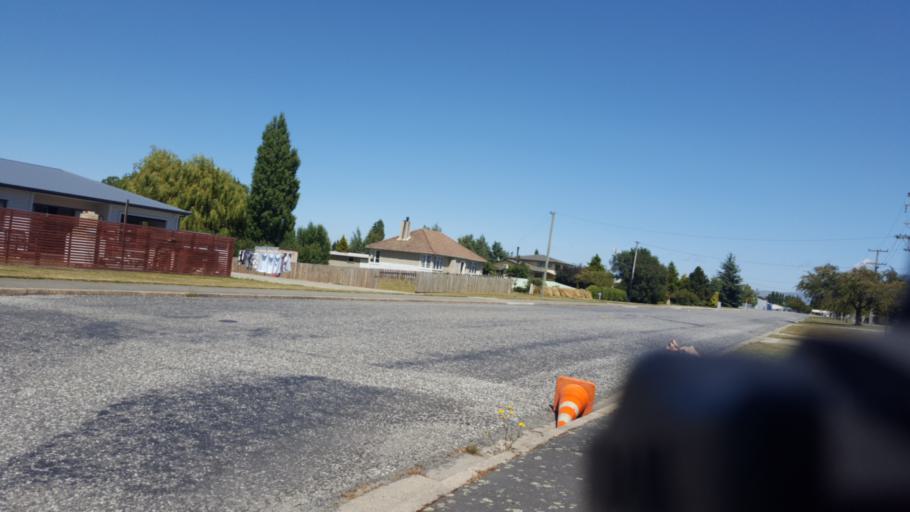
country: NZ
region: Otago
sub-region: Dunedin City
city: Dunedin
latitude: -45.1291
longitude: 170.1059
